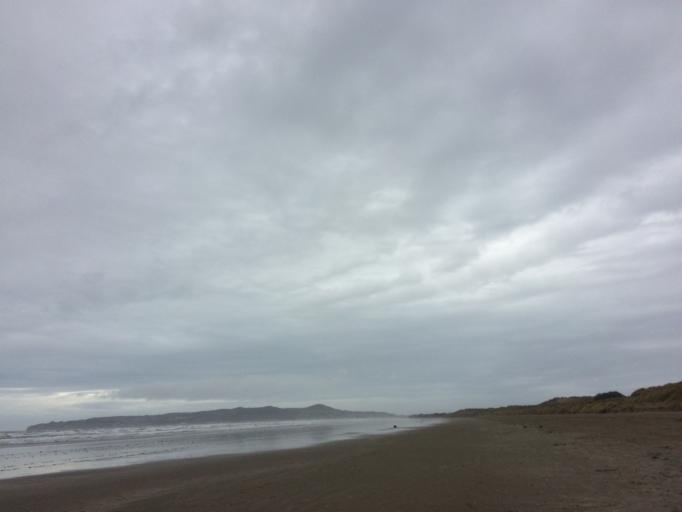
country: IE
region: Leinster
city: Portmarnock
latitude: 53.4239
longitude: -6.1224
